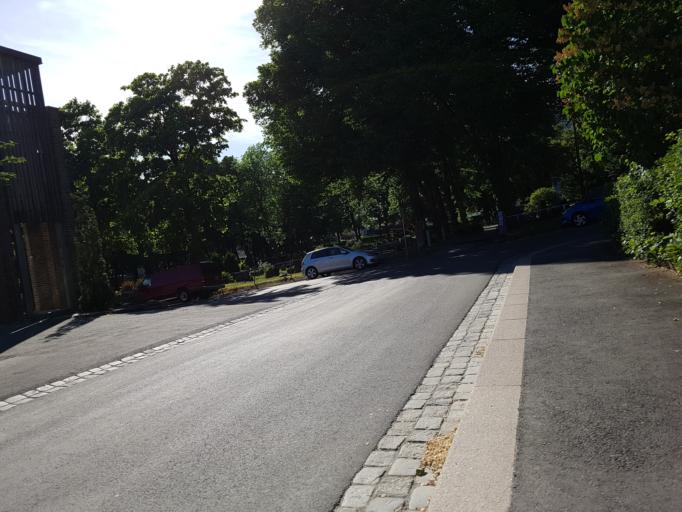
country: NO
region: Buskerud
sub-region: Drammen
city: Drammen
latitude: 59.7471
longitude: 10.2039
